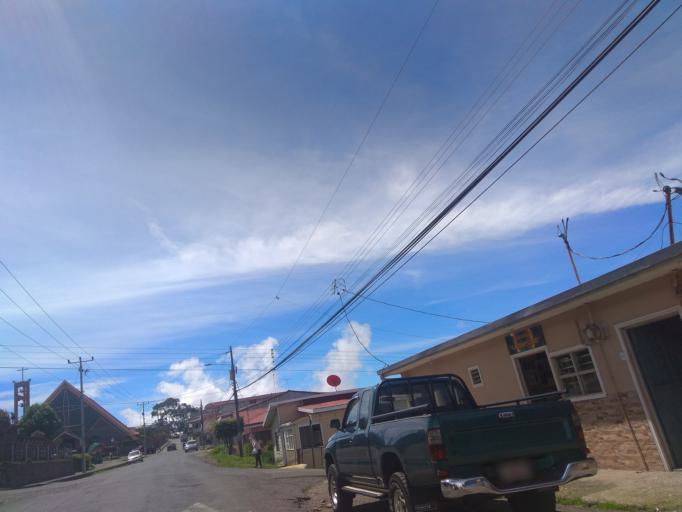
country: CR
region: Cartago
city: Cot
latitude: 9.9153
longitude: -83.8944
